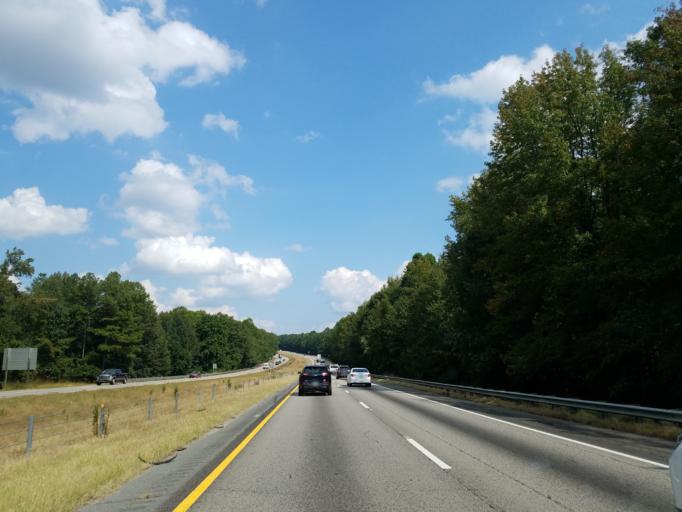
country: US
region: Georgia
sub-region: Gwinnett County
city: Dacula
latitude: 34.0766
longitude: -83.8971
